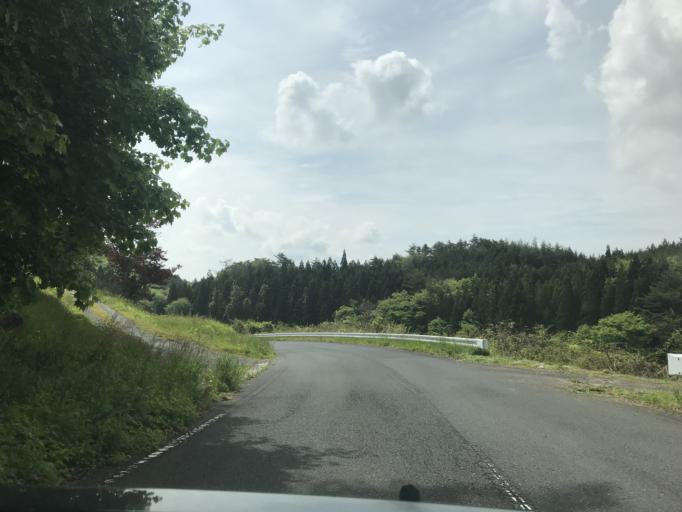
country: JP
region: Iwate
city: Ichinoseki
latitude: 38.8767
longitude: 140.9760
